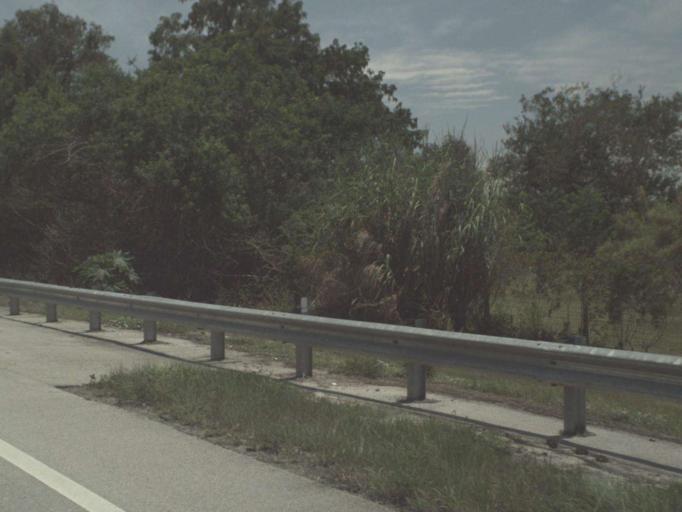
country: US
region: Florida
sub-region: Okeechobee County
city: Taylor Creek
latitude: 27.1112
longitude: -80.6642
